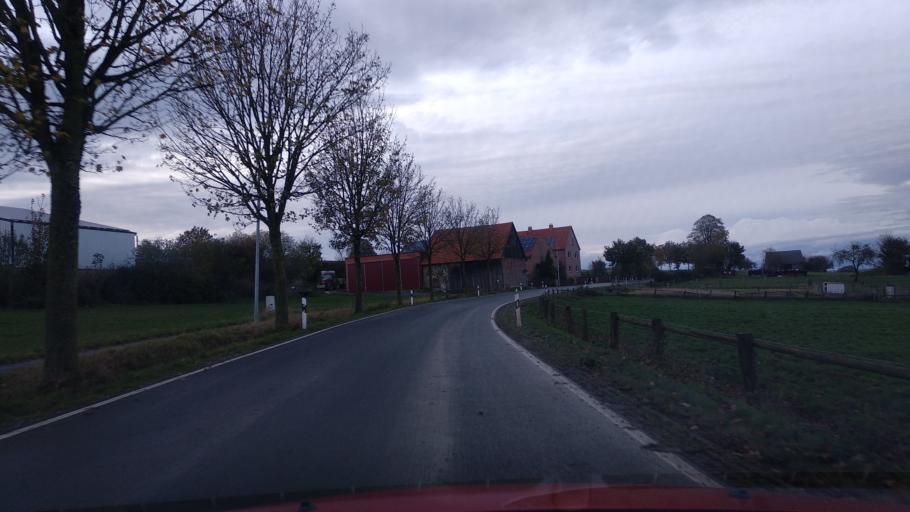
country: DE
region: North Rhine-Westphalia
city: Borgentreich
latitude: 51.6596
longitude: 9.2706
